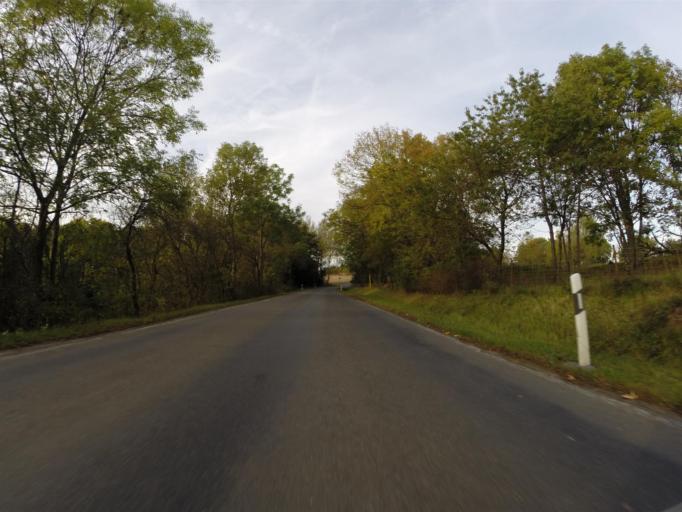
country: DE
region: Thuringia
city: Lehesten
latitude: 50.9683
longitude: 11.5979
